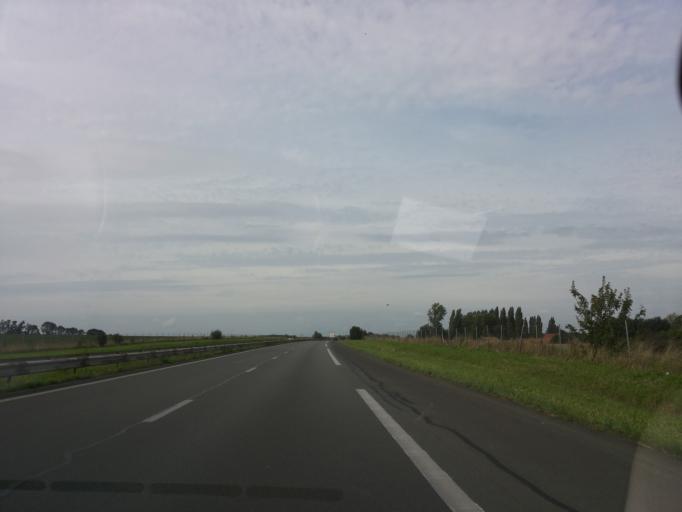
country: FR
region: Nord-Pas-de-Calais
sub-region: Departement du Pas-de-Calais
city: Allouagne
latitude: 50.5428
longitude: 2.4922
